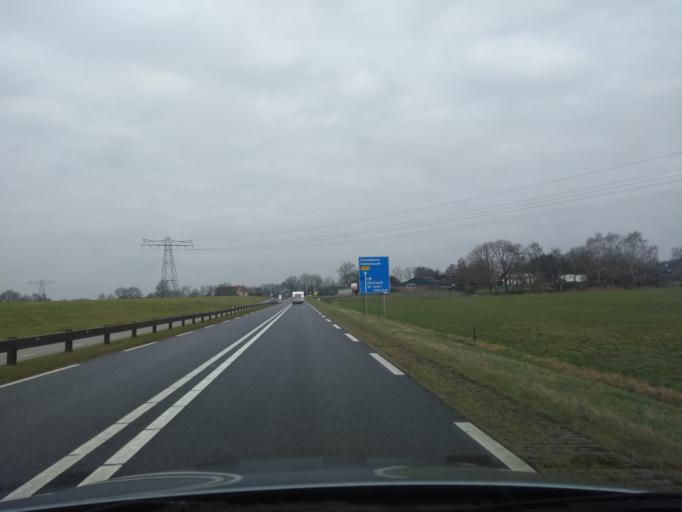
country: NL
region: Overijssel
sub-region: Gemeente Steenwijkerland
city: Sint Jansklooster
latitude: 52.6530
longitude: 6.0110
